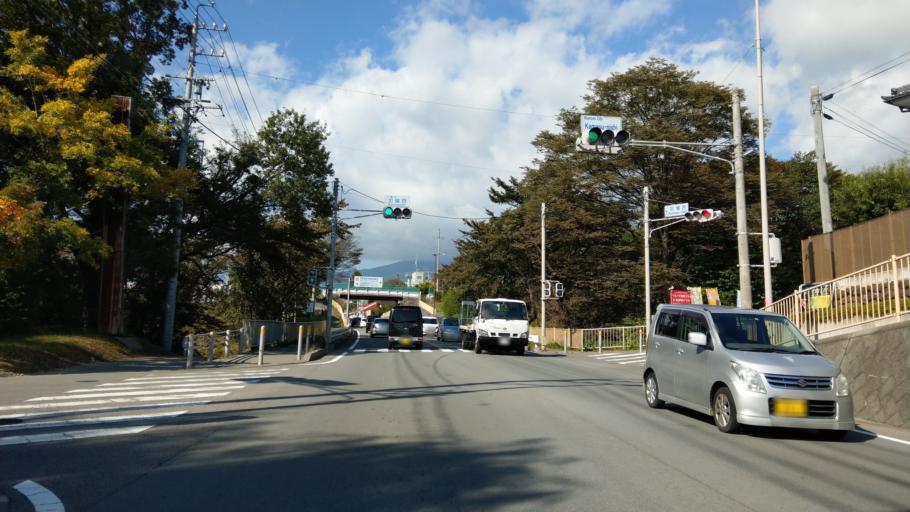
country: JP
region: Nagano
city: Komoro
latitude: 36.3233
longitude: 138.4363
